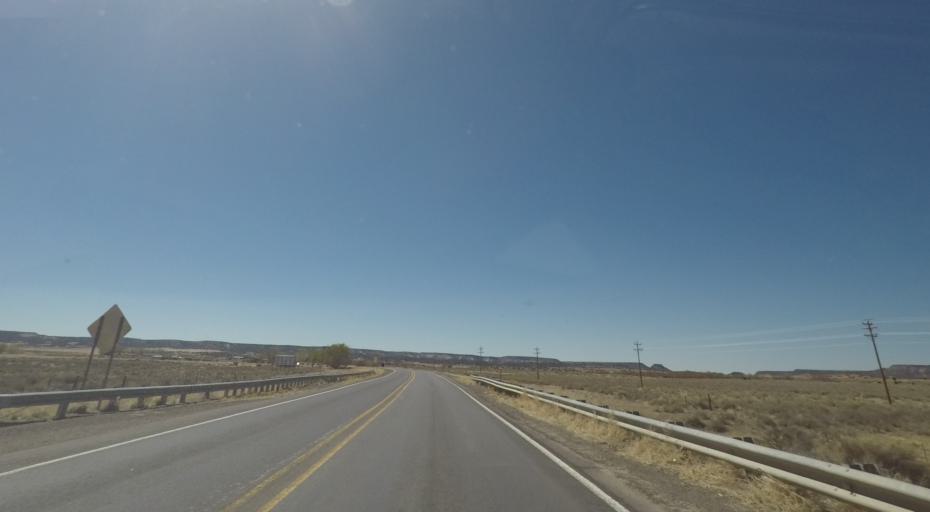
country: US
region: New Mexico
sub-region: Catron County
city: Reserve
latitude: 34.3441
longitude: -108.5009
